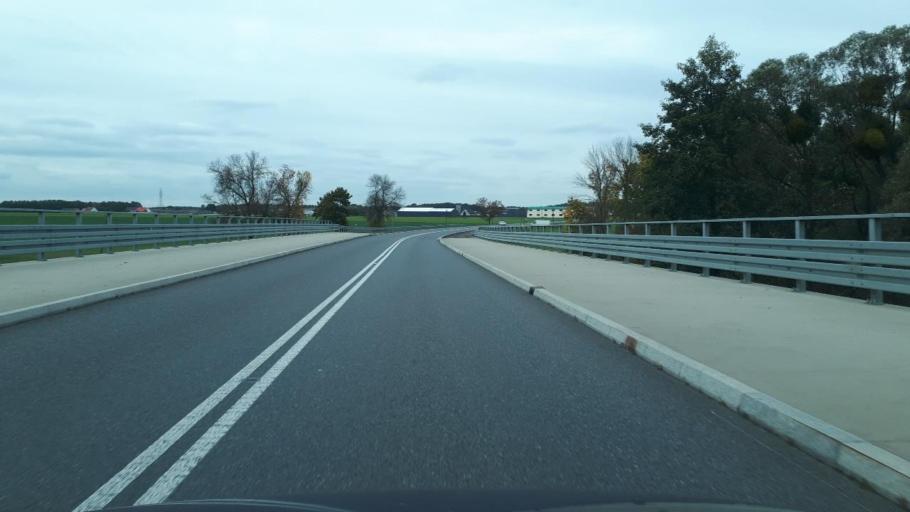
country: PL
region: Opole Voivodeship
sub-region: Powiat oleski
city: Dobrodzien
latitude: 50.7549
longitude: 18.4333
